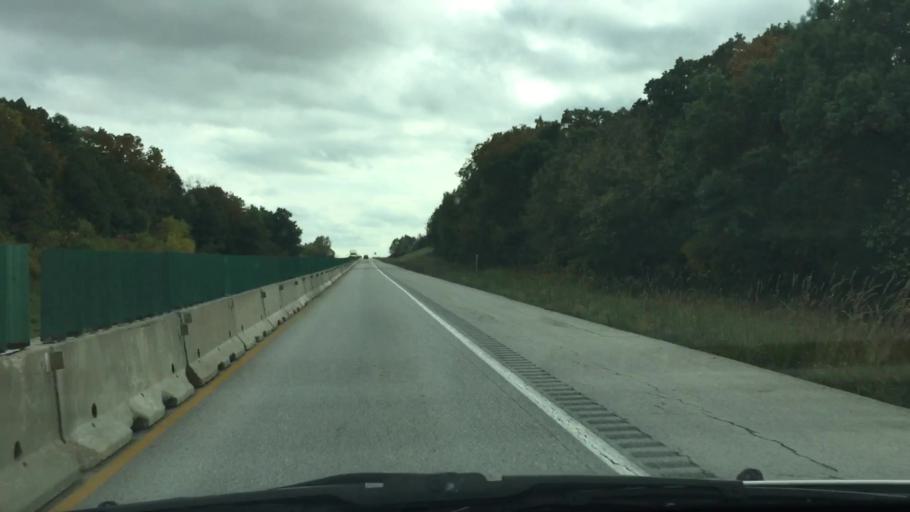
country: US
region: Iowa
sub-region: Decatur County
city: Leon
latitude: 40.6960
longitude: -93.8461
